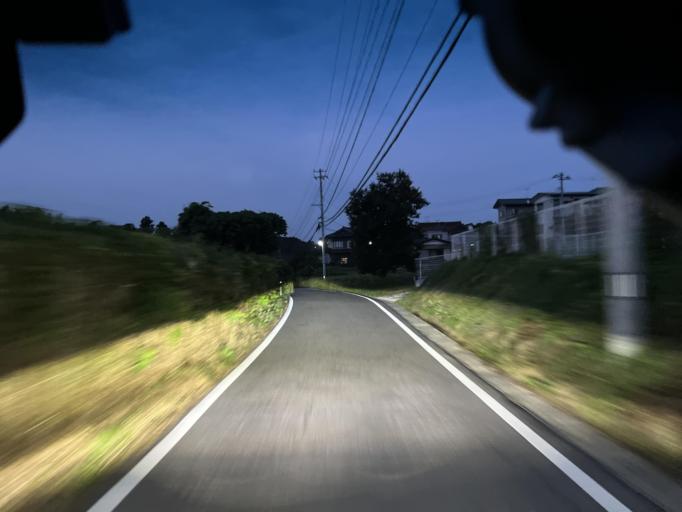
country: JP
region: Fukushima
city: Koriyama
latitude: 37.4158
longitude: 140.4263
